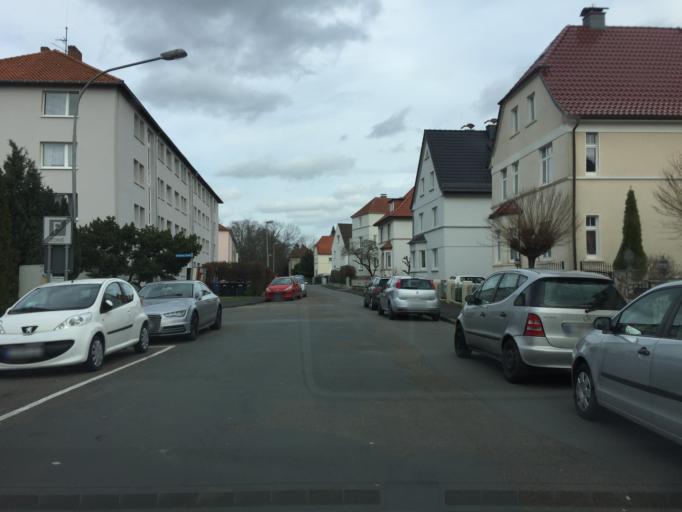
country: DE
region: North Rhine-Westphalia
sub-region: Regierungsbezirk Detmold
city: Detmold
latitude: 51.9466
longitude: 8.8770
